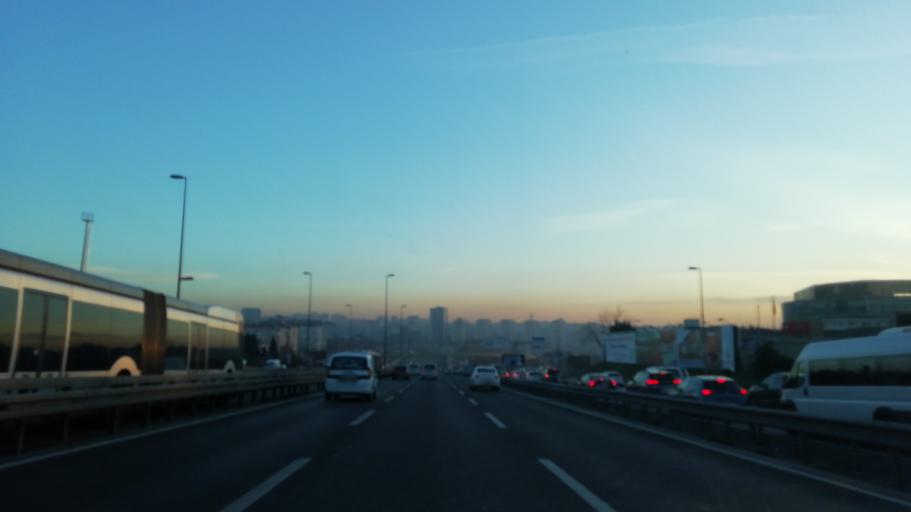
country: TR
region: Istanbul
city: guengoeren merter
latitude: 41.0002
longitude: 28.8812
